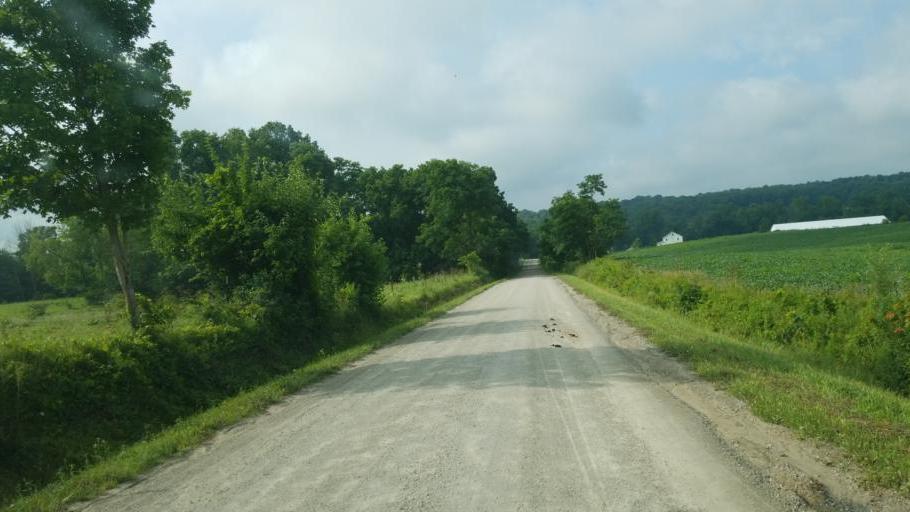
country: US
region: Ohio
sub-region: Knox County
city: Fredericktown
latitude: 40.5478
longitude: -82.6428
